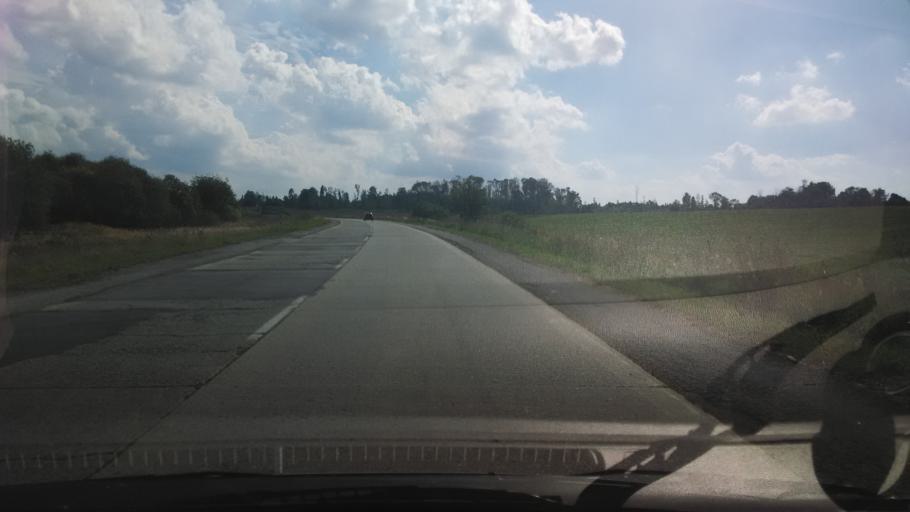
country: SK
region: Zilinsky
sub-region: Okres Martin
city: Martin
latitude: 48.9513
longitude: 18.8954
